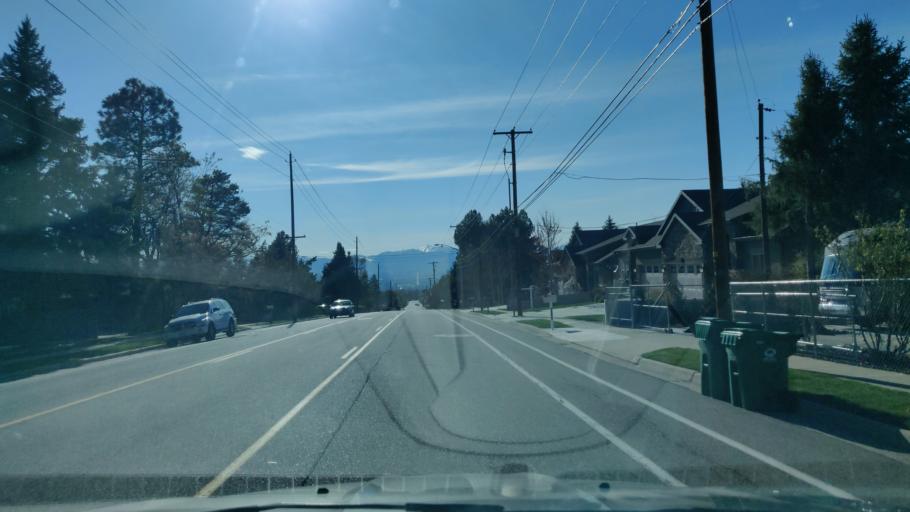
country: US
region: Utah
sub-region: Salt Lake County
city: Cottonwood Heights
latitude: 40.6094
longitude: -111.8009
